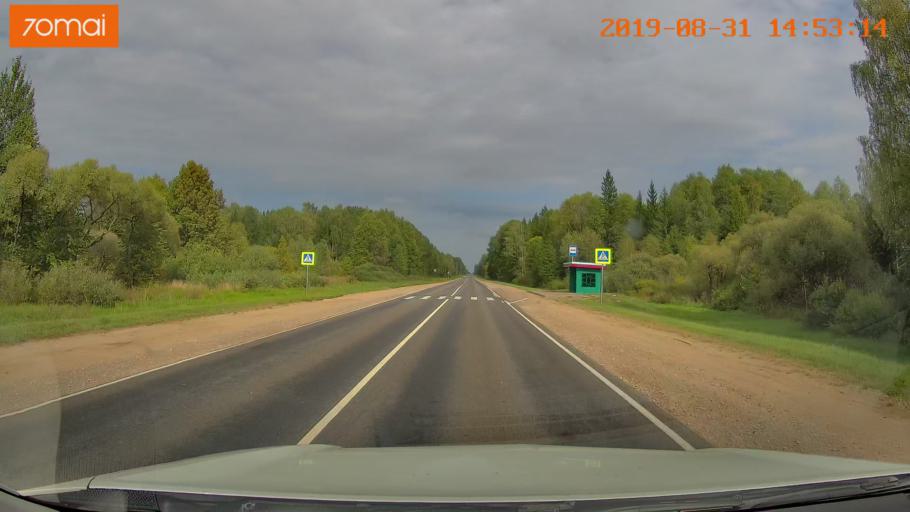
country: RU
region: Kaluga
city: Spas-Demensk
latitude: 54.2818
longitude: 33.8593
